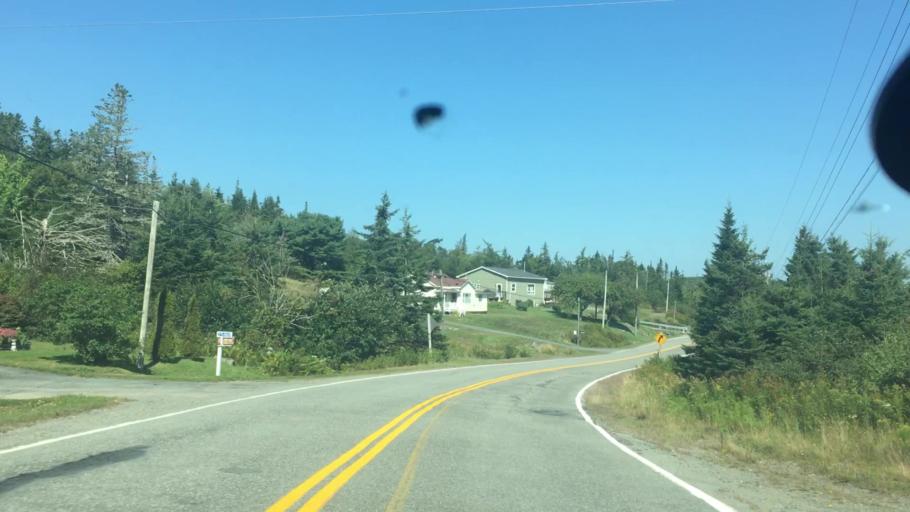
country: CA
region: Nova Scotia
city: New Glasgow
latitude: 44.9148
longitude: -62.3845
